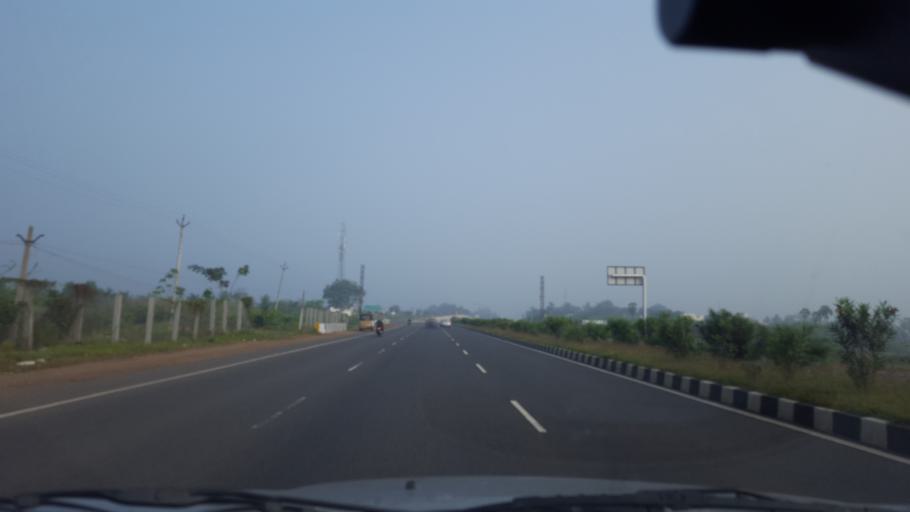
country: IN
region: Andhra Pradesh
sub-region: Prakasam
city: Ongole
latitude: 15.4171
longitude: 80.0393
